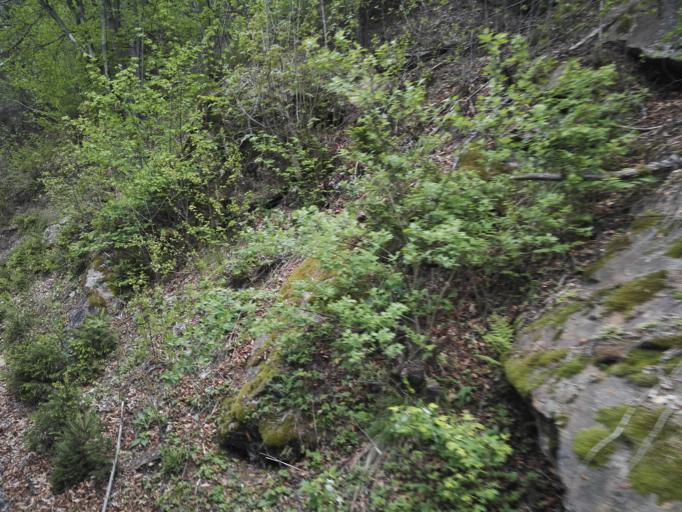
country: AT
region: Styria
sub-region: Politischer Bezirk Weiz
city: Birkfeld
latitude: 47.3426
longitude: 15.7005
